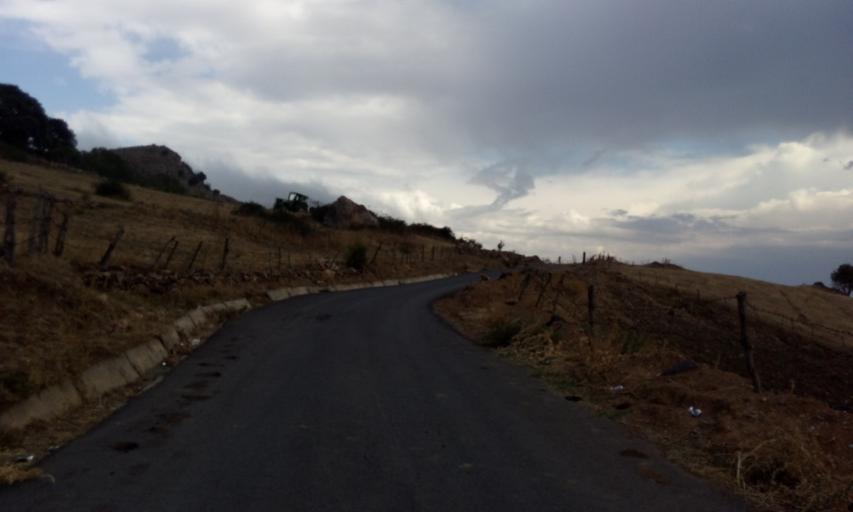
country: DZ
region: Tizi Ouzou
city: Chemini
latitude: 36.6037
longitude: 4.5733
